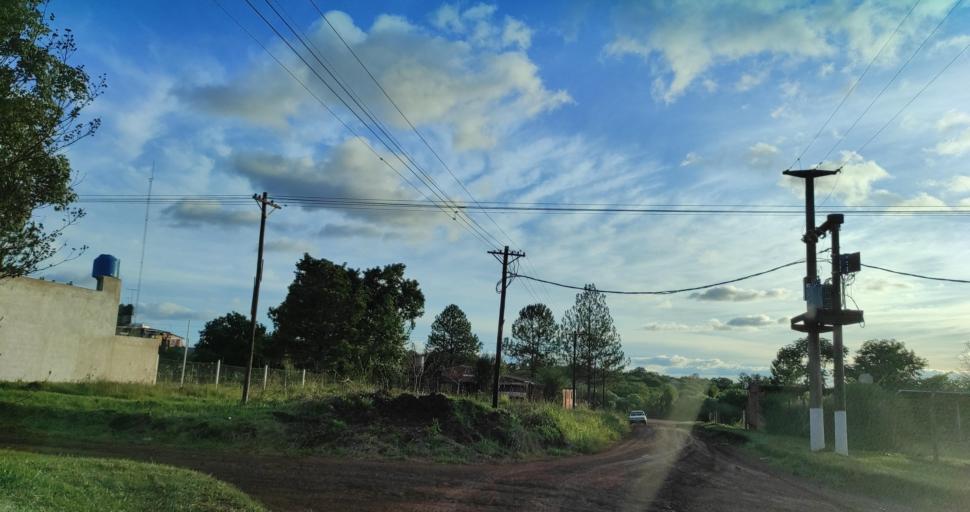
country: AR
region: Misiones
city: Garupa
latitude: -27.5234
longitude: -55.8573
